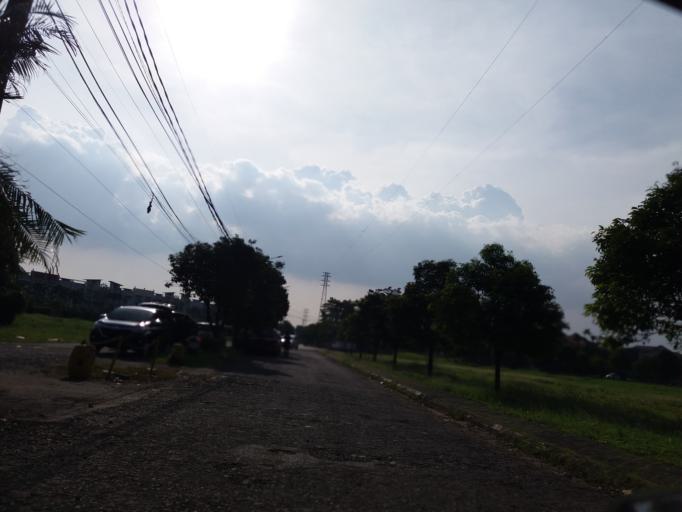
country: ID
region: West Java
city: Bandung
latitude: -6.9624
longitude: 107.6264
